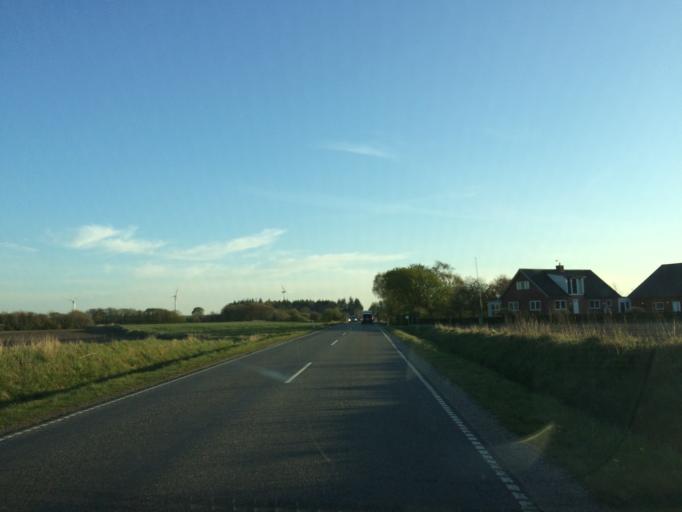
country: DK
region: Central Jutland
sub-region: Struer Kommune
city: Struer
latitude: 56.4347
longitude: 8.5207
